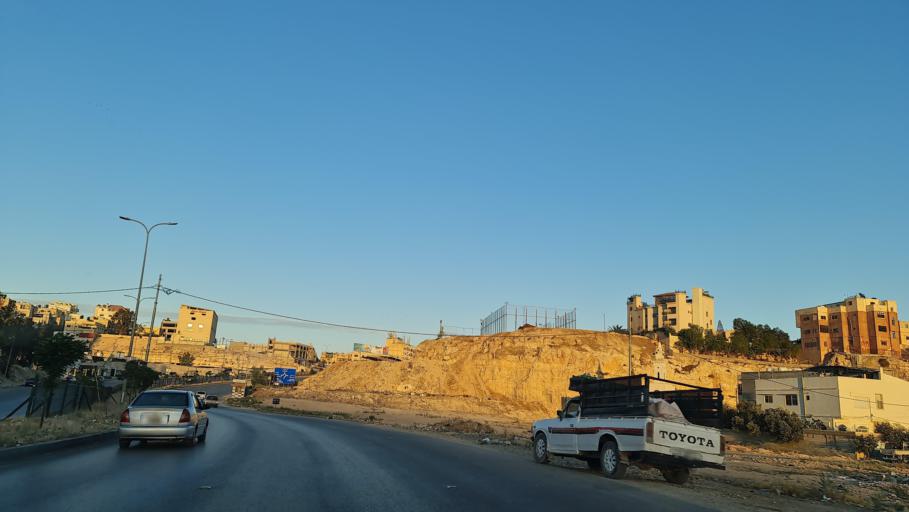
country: JO
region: Zarqa
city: Zarqa
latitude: 32.0799
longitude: 36.0707
